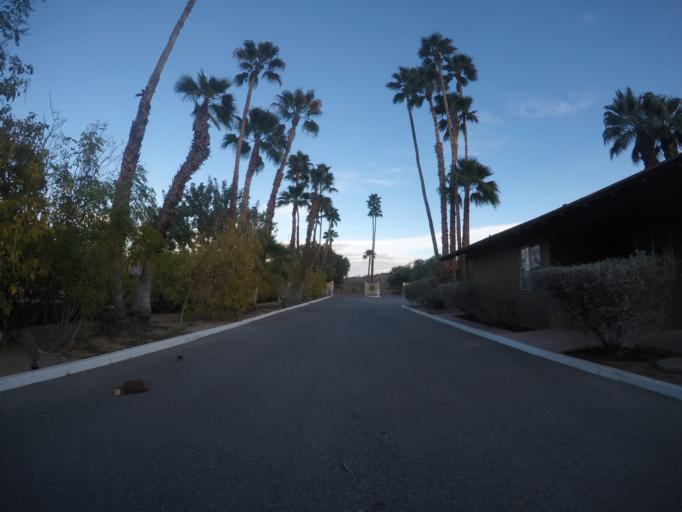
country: US
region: California
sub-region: Riverside County
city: Palm Springs
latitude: 33.7993
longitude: -116.5281
